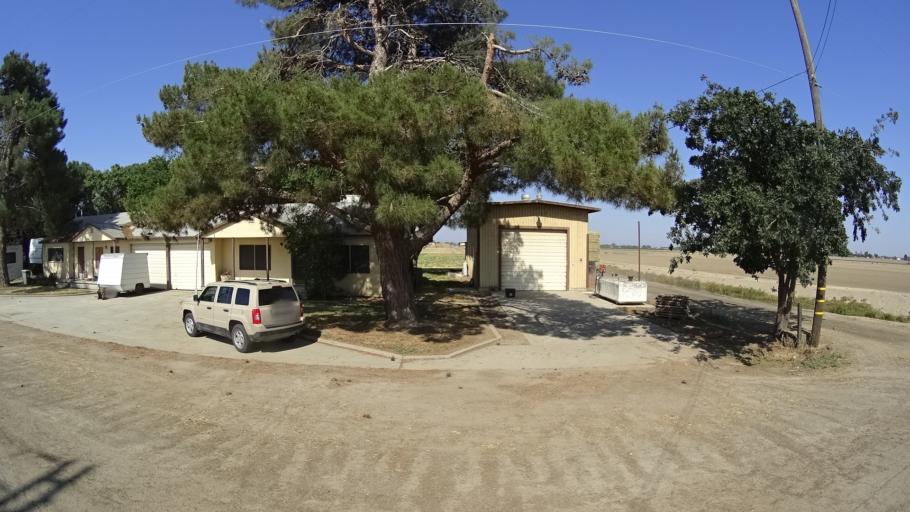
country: US
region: California
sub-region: Kings County
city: Home Garden
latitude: 36.3354
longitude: -119.5651
